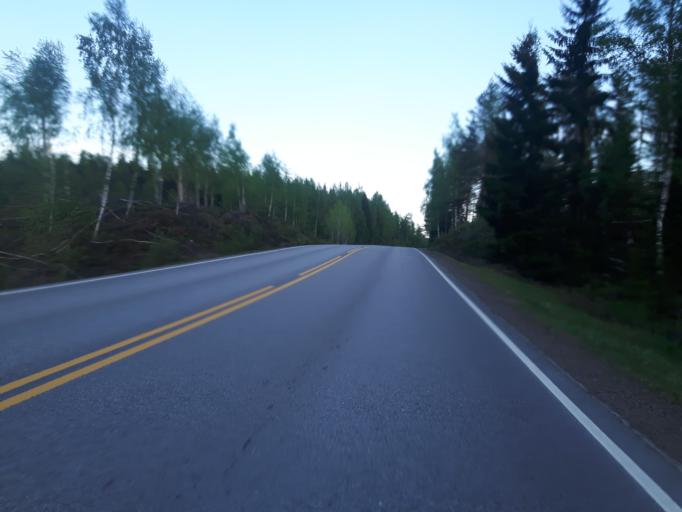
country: FI
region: Uusimaa
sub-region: Loviisa
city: Perna
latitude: 60.4581
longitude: 26.0761
